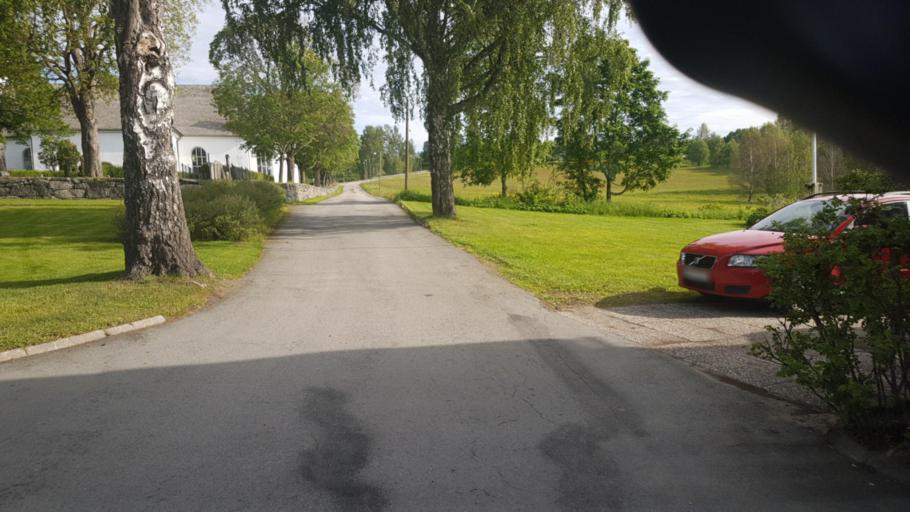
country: SE
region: Vaermland
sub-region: Arvika Kommun
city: Arvika
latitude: 59.8111
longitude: 12.5654
